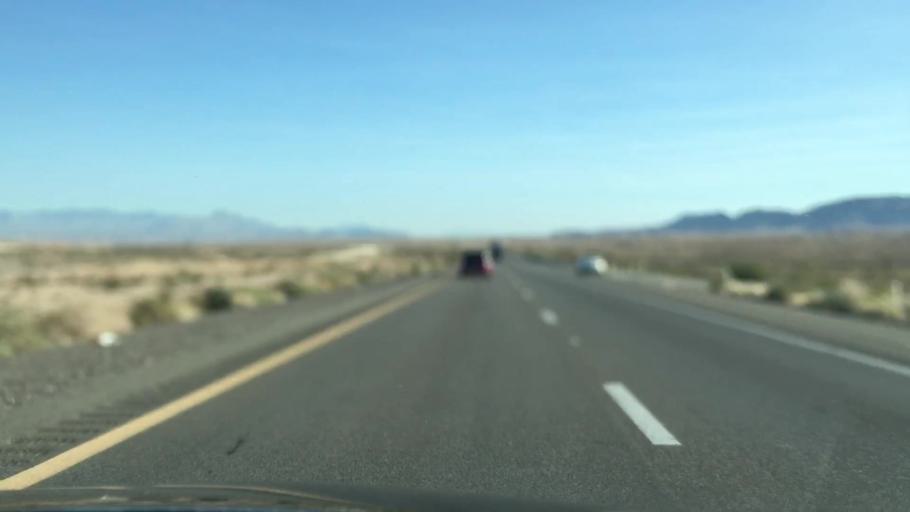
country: US
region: Nevada
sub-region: Clark County
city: Moapa Town
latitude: 36.5534
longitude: -114.6943
